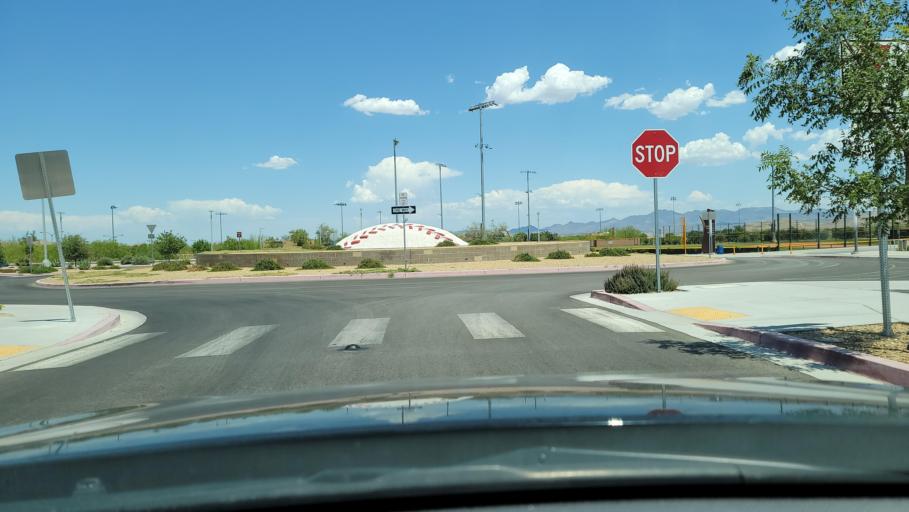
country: US
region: Nevada
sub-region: Clark County
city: Enterprise
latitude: 36.0043
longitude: -115.2716
